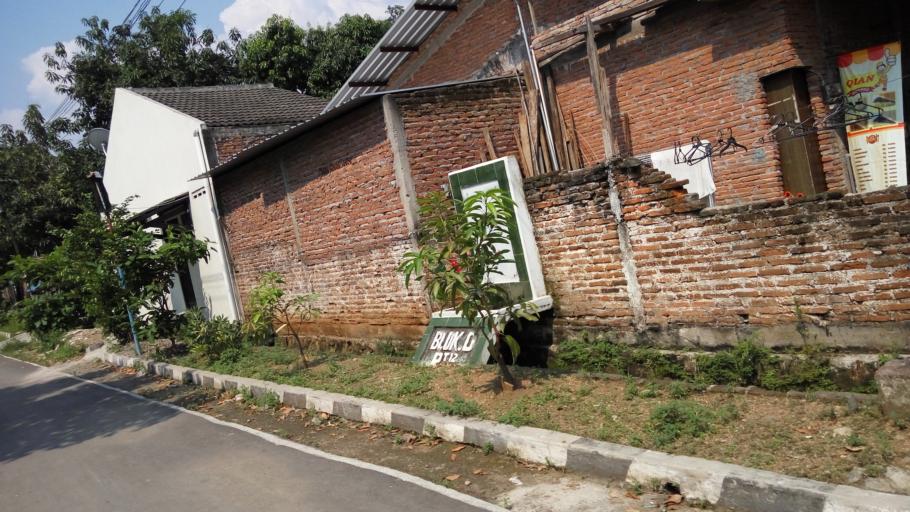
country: ID
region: Central Java
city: Mranggen
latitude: -7.0345
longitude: 110.4739
